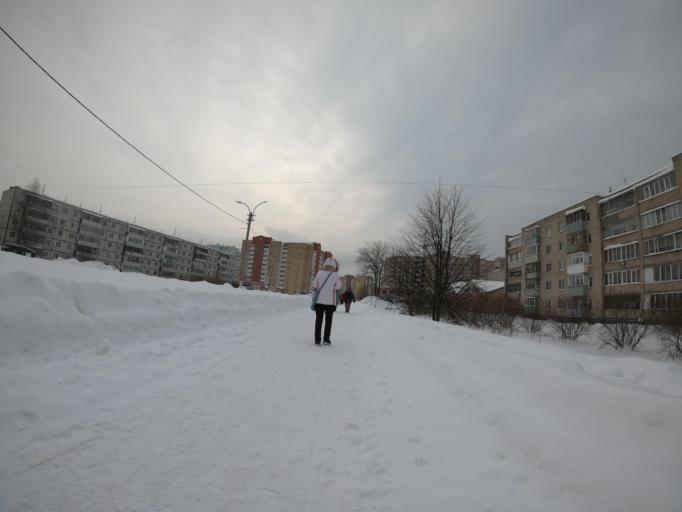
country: RU
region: Moskovskaya
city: Elektrogorsk
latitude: 55.8854
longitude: 38.7743
